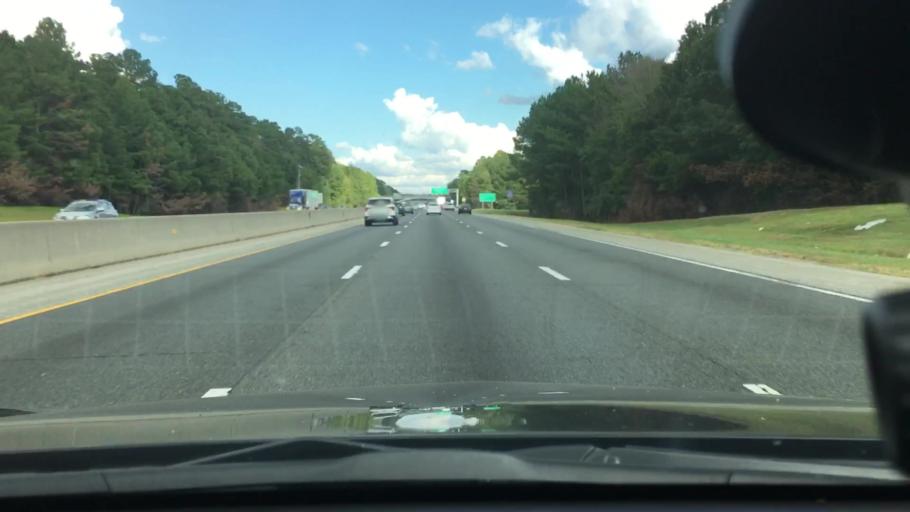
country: US
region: North Carolina
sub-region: Orange County
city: Chapel Hill
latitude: 35.9053
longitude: -78.9534
